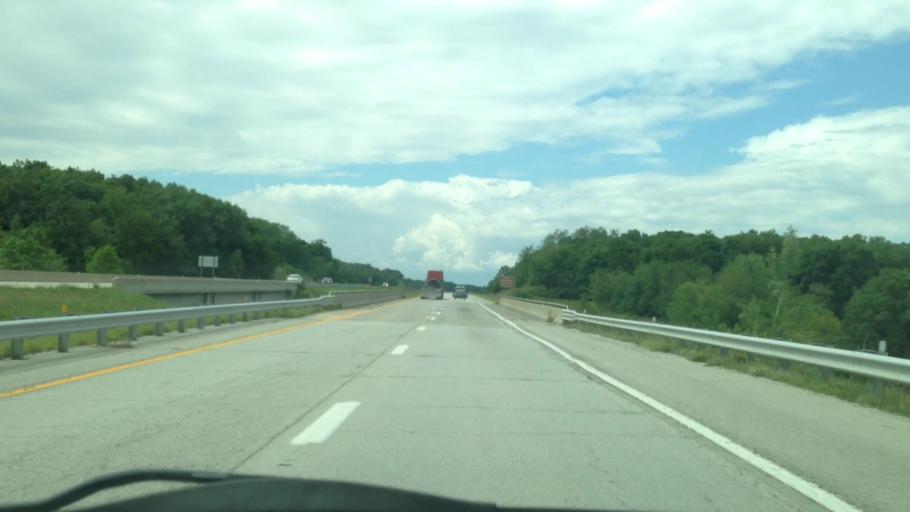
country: US
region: Missouri
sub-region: Pike County
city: Bowling Green
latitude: 39.3506
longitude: -91.1897
